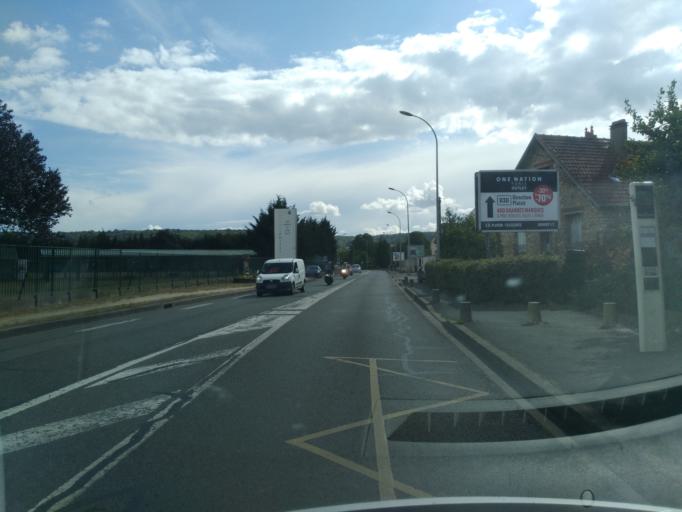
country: FR
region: Ile-de-France
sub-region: Departement des Yvelines
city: Chambourcy
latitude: 48.9179
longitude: 2.0261
